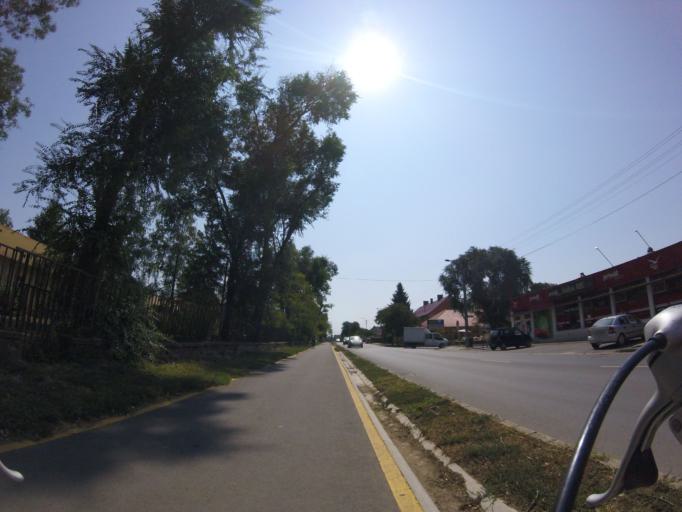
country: HU
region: Szabolcs-Szatmar-Bereg
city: Kisvarda
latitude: 48.2073
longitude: 22.0887
